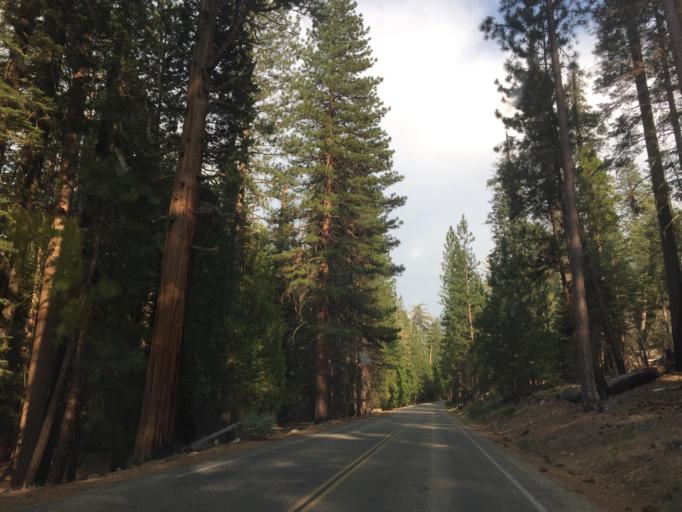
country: US
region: California
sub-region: Tulare County
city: Three Rivers
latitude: 36.7945
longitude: -118.6846
